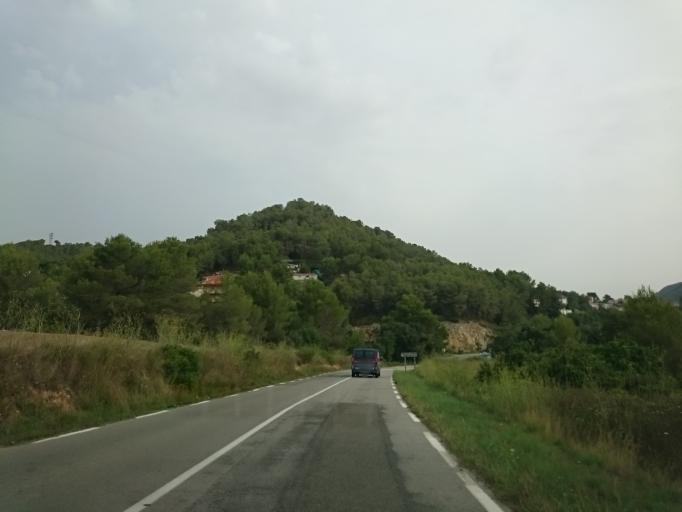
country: ES
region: Catalonia
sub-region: Provincia de Barcelona
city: Sant Pere de Ribes
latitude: 41.2885
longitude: 1.7761
